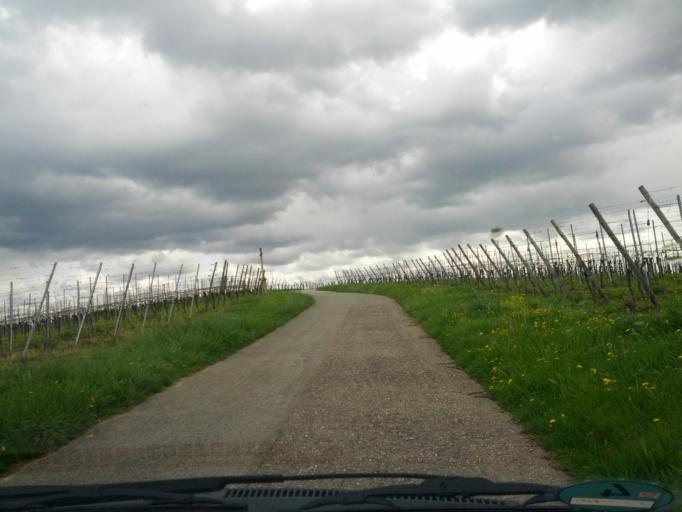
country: DE
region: Baden-Wuerttemberg
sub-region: Freiburg Region
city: Pfaffenweiler
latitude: 47.9425
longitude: 7.7467
